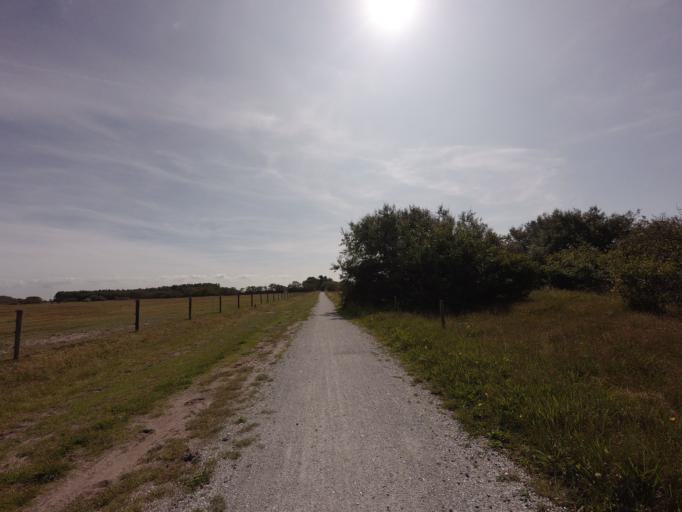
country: NL
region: Friesland
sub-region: Gemeente Ameland
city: Hollum
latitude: 53.4473
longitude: 5.6554
